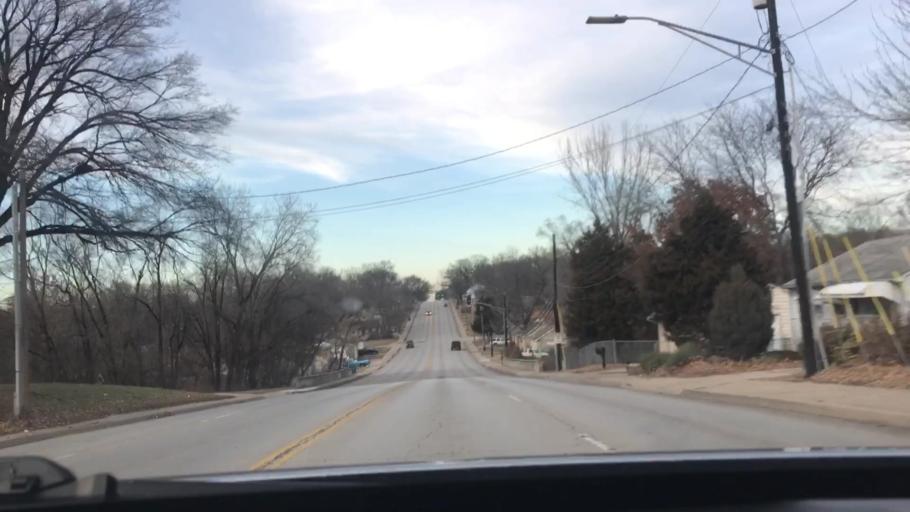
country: US
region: Missouri
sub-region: Jackson County
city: Independence
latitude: 39.0736
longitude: -94.4463
